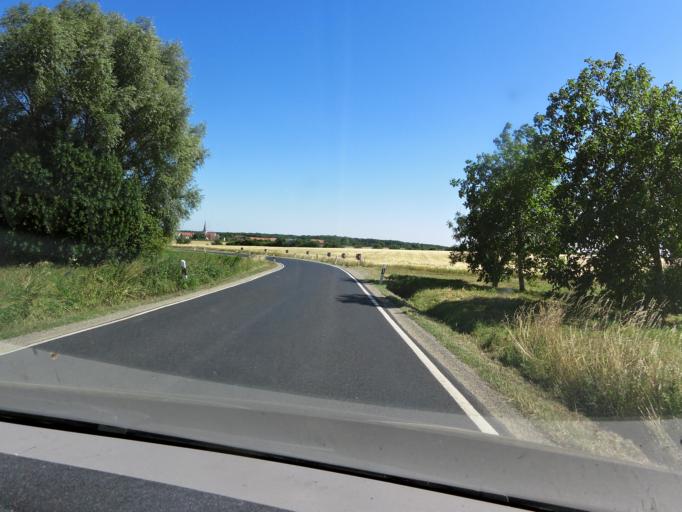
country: DE
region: Bavaria
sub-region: Regierungsbezirk Unterfranken
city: Biebelried
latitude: 49.7358
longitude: 10.0801
